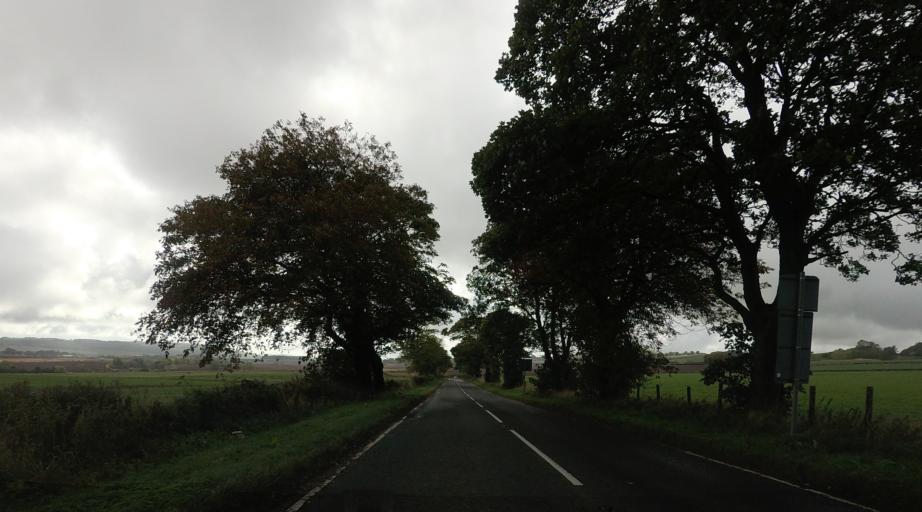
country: GB
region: Scotland
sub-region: Fife
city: Balmullo
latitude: 56.3732
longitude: -2.9296
